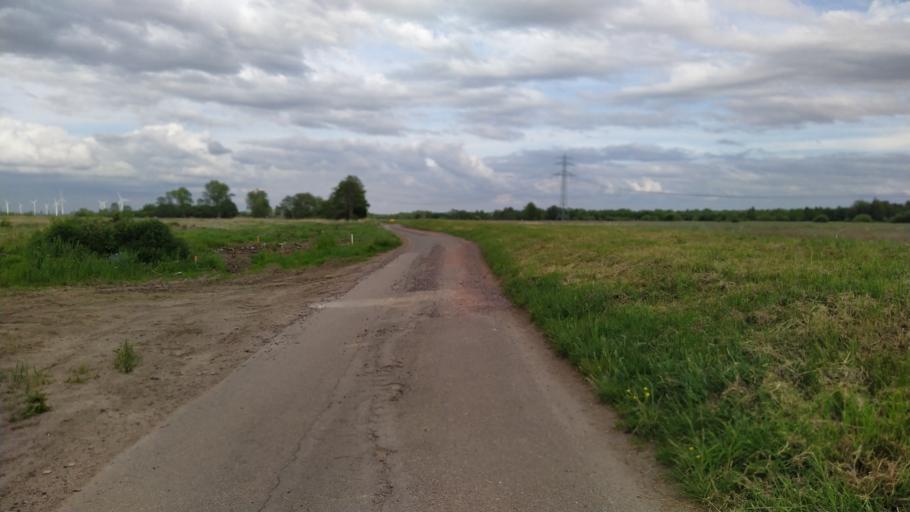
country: DE
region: Lower Saxony
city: Neu Wulmstorf
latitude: 53.4945
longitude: 9.7941
